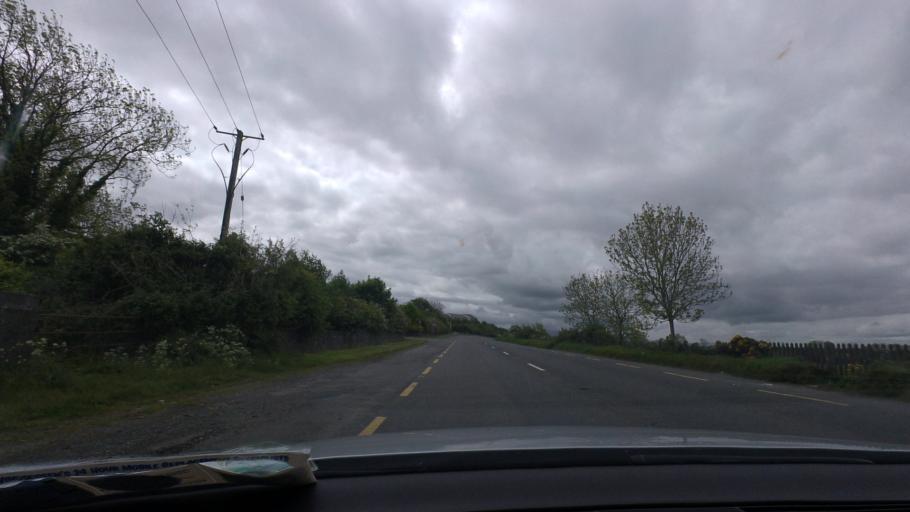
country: IE
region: Munster
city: Cashel
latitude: 52.5376
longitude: -7.8731
